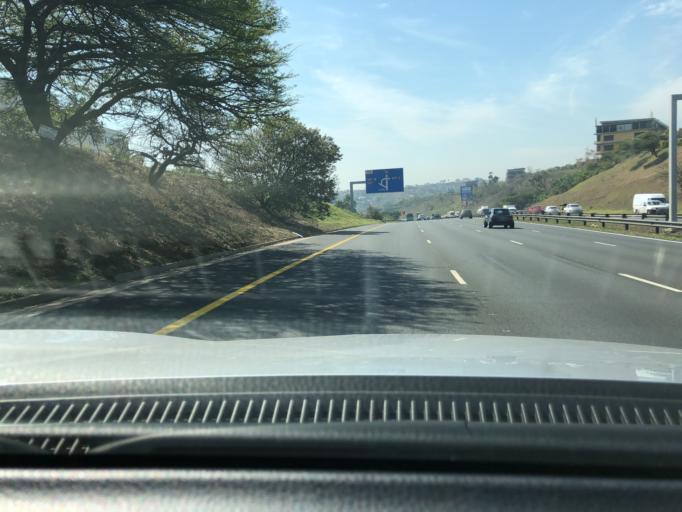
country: ZA
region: KwaZulu-Natal
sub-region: eThekwini Metropolitan Municipality
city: Berea
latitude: -29.8299
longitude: 30.9619
